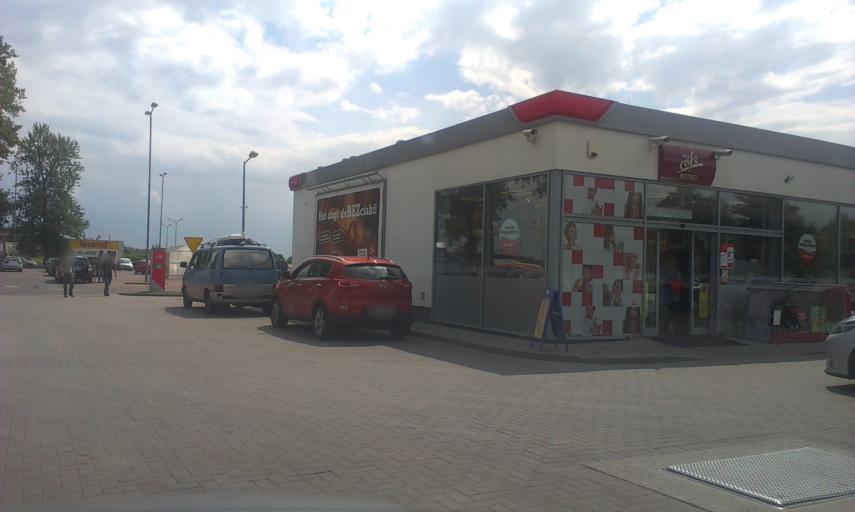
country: PL
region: West Pomeranian Voivodeship
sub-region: Powiat bialogardzki
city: Bialogard
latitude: 53.9989
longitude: 15.9912
